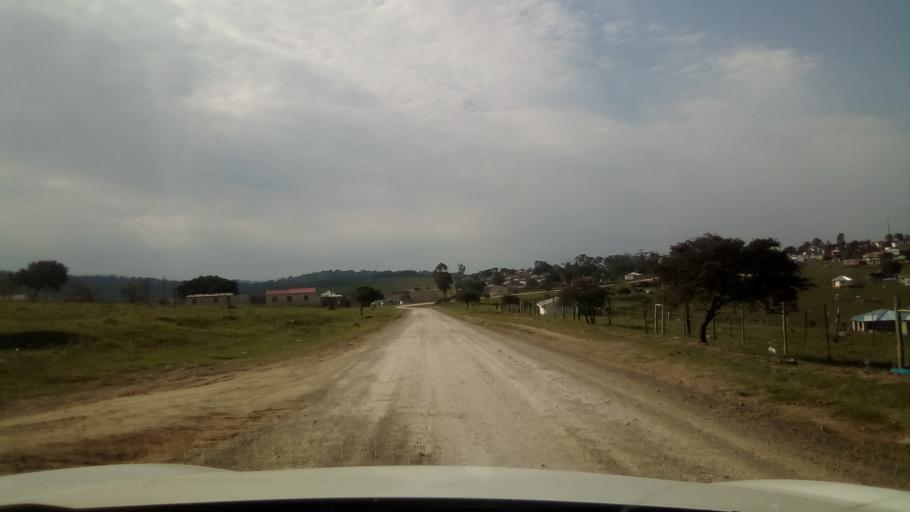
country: ZA
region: Eastern Cape
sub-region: Buffalo City Metropolitan Municipality
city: Bhisho
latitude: -32.9859
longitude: 27.2609
